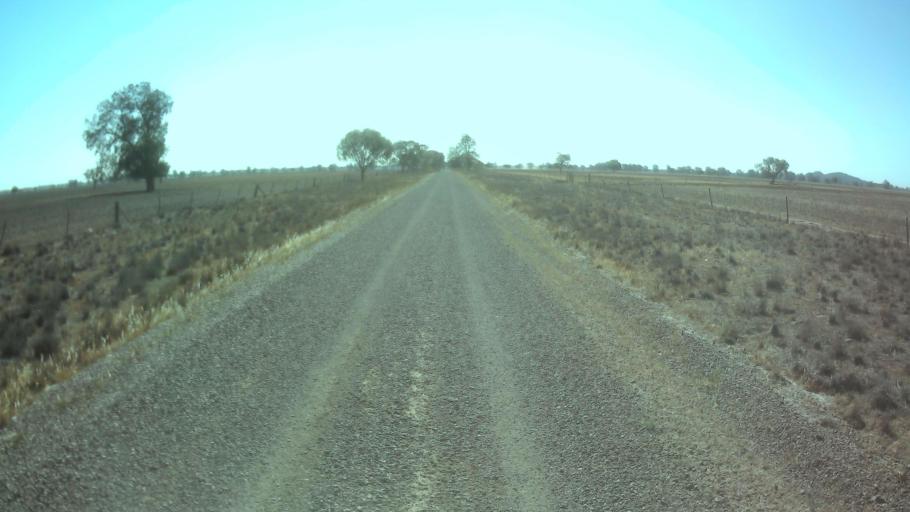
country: AU
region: New South Wales
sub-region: Weddin
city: Grenfell
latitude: -33.7603
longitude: 147.7119
